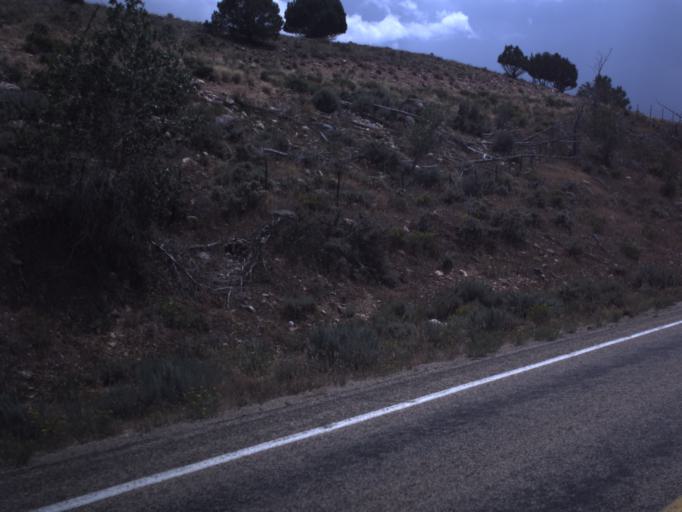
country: US
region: Utah
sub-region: Summit County
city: Francis
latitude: 40.4539
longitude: -110.8195
